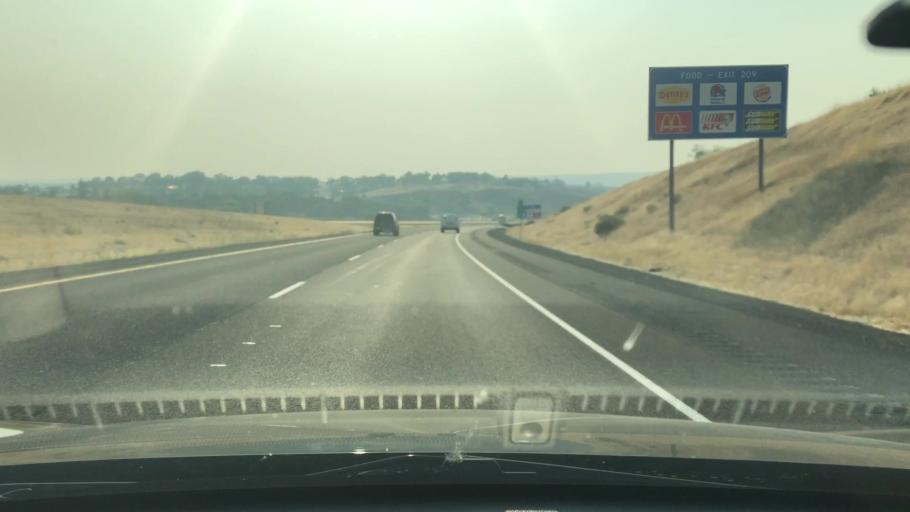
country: US
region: Oregon
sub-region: Umatilla County
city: Pendleton
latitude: 45.6611
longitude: -118.7966
